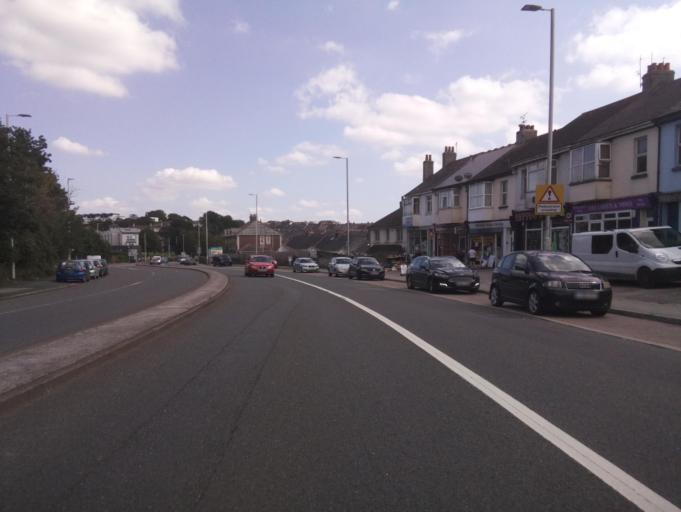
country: GB
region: England
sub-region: Plymouth
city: Plymouth
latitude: 50.3874
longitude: -4.1638
